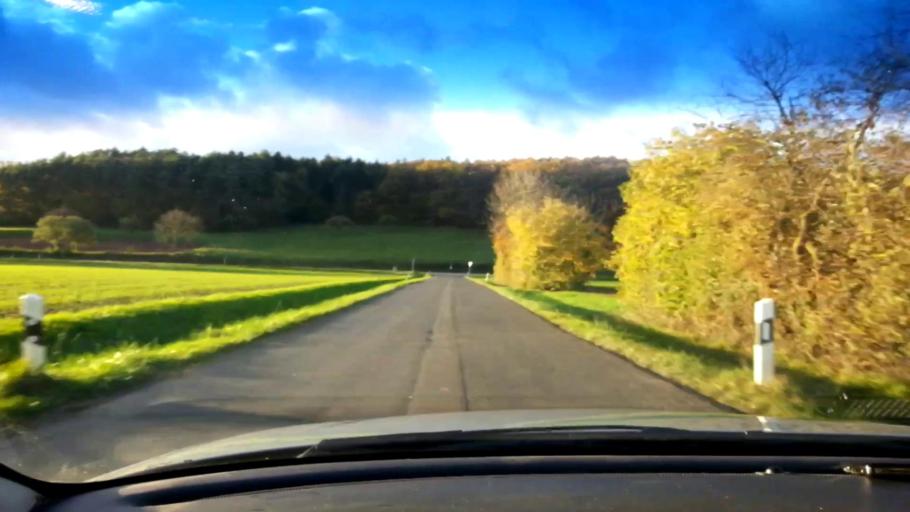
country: DE
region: Bavaria
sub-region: Upper Franconia
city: Zapfendorf
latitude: 50.0408
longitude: 10.9243
